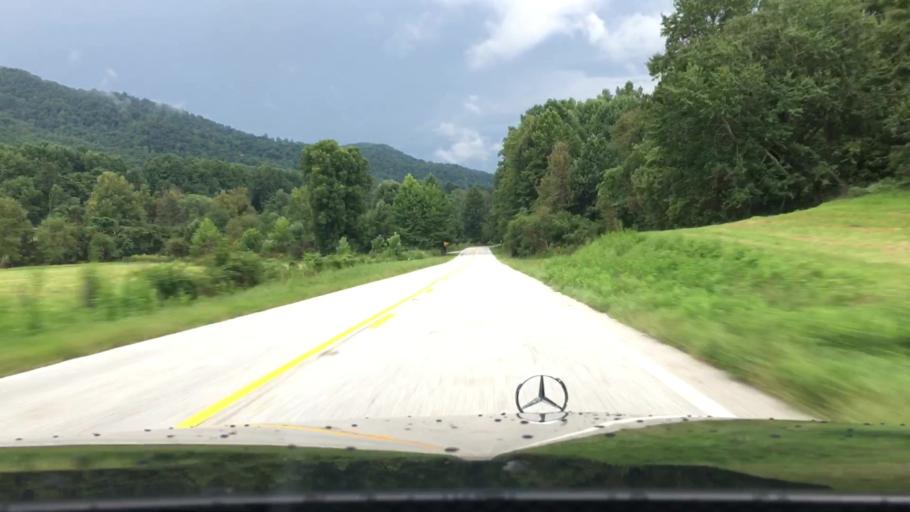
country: US
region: Virginia
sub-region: Nelson County
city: Lovingston
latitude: 37.8207
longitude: -78.9359
